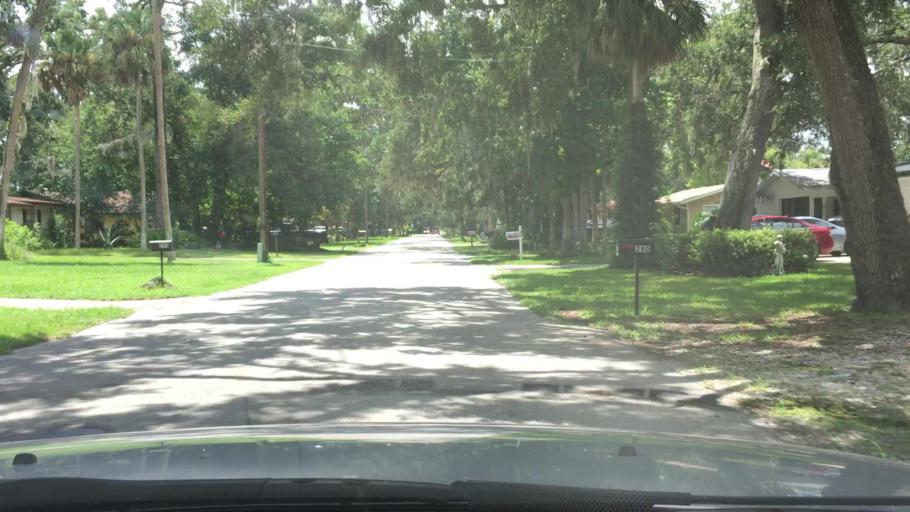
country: US
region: Florida
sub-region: Volusia County
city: Ormond Beach
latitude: 29.2703
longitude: -81.0655
